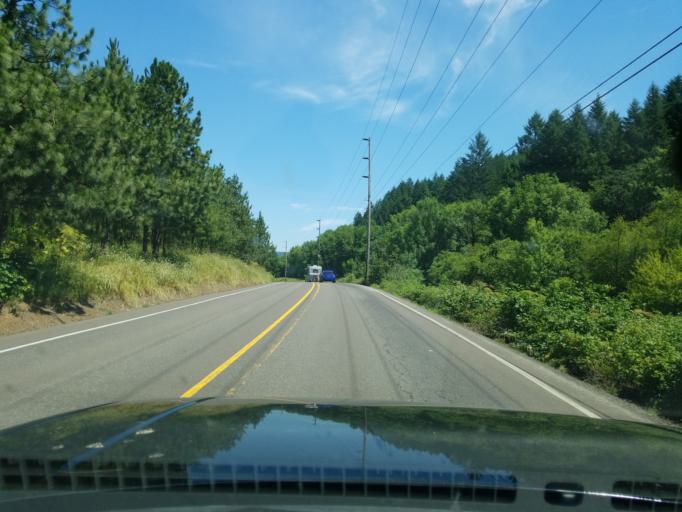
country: US
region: Oregon
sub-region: Yamhill County
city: Yamhill
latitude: 45.3835
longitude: -123.1408
